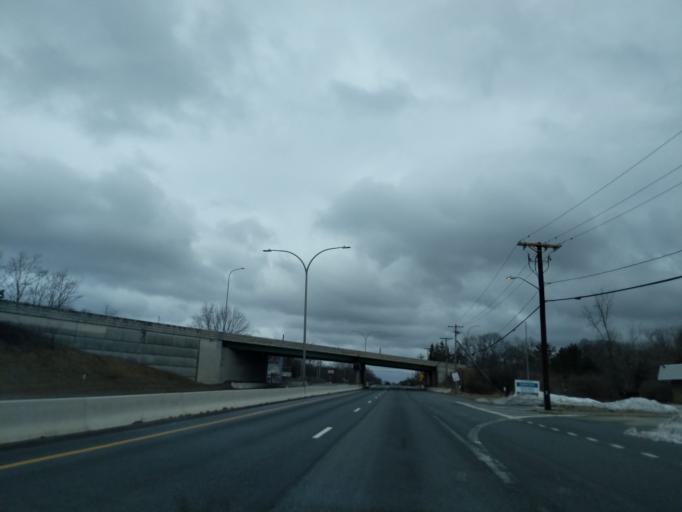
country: US
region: Rhode Island
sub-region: Providence County
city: Cumberland Hill
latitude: 41.9500
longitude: -71.4842
